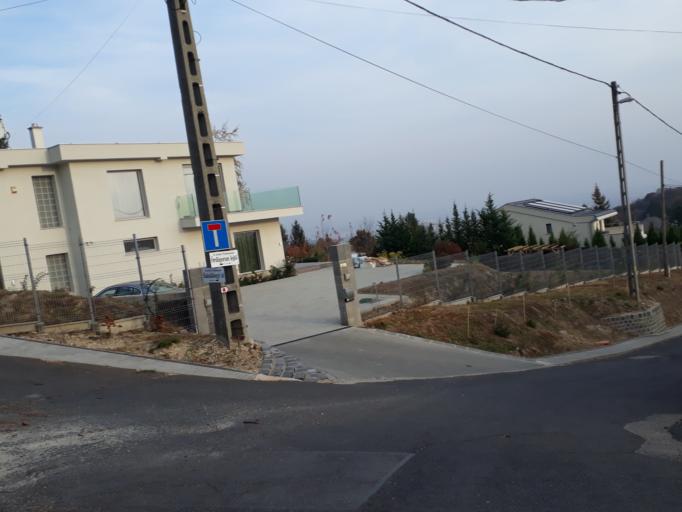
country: HU
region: Pest
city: Budaors
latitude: 47.4769
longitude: 18.9759
